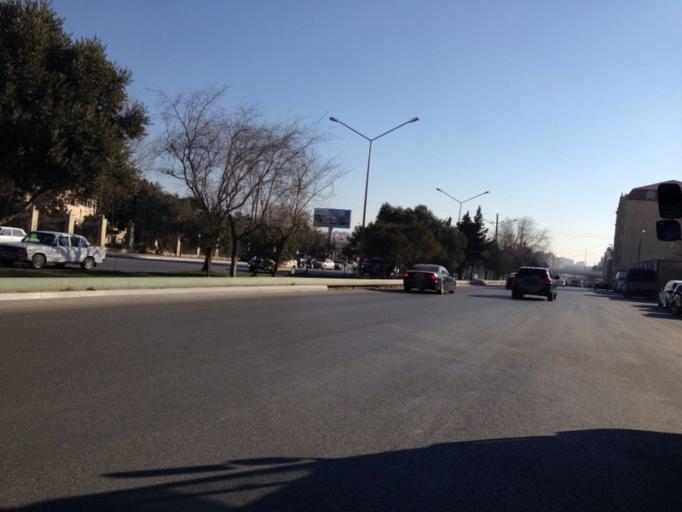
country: AZ
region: Baki
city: Baku
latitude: 40.4187
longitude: 49.8563
